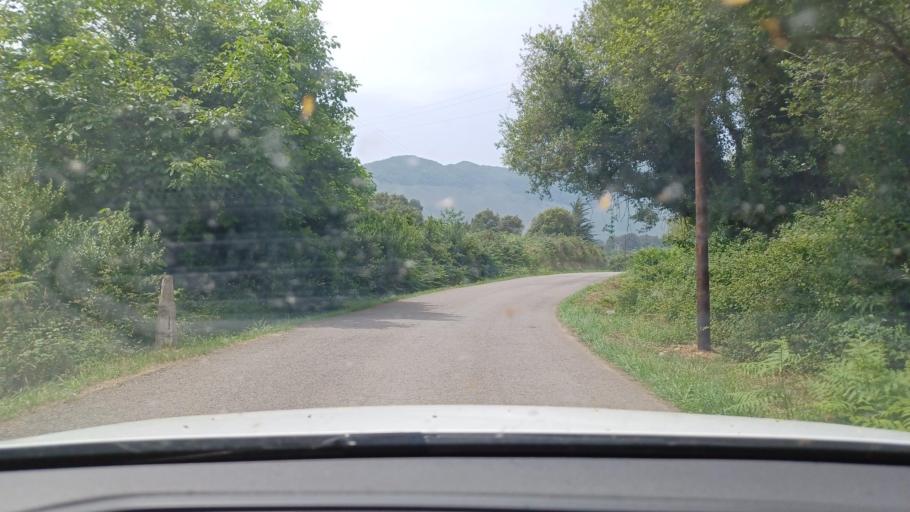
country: ES
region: Asturias
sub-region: Province of Asturias
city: Ribadesella
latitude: 43.4476
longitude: -4.9788
